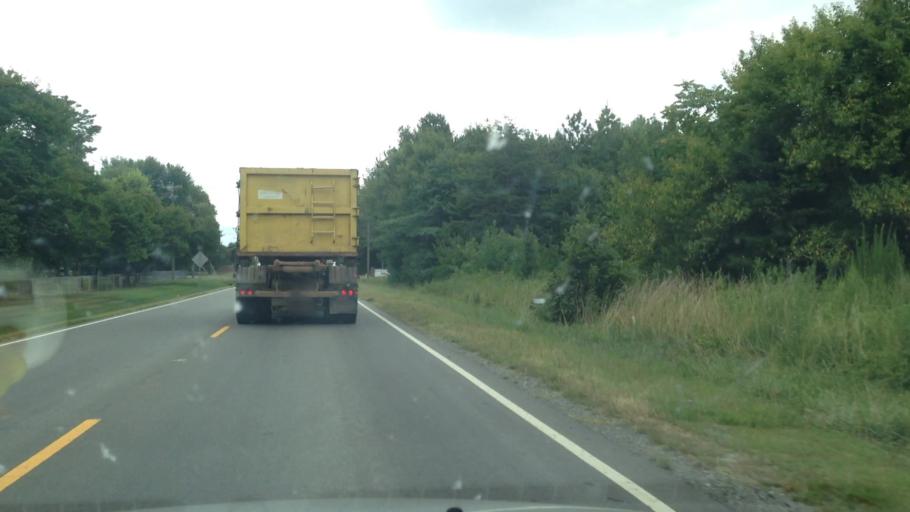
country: US
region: North Carolina
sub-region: Rockingham County
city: Wentworth
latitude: 36.3703
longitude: -79.7266
